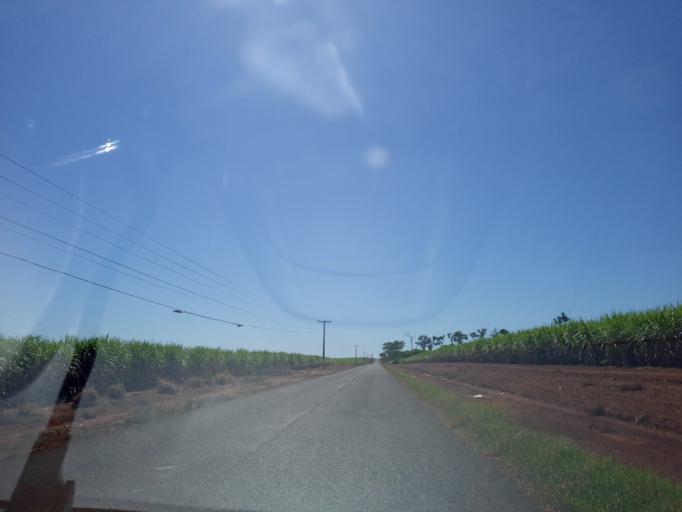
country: BR
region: Goias
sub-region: Itumbiara
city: Itumbiara
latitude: -18.4260
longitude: -49.1769
